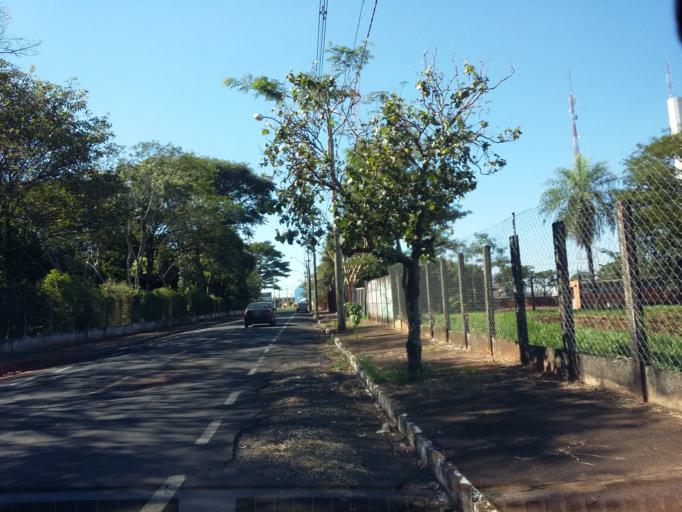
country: BR
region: Sao Paulo
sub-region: Sao Jose Do Rio Preto
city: Sao Jose do Rio Preto
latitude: -20.8345
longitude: -49.3609
